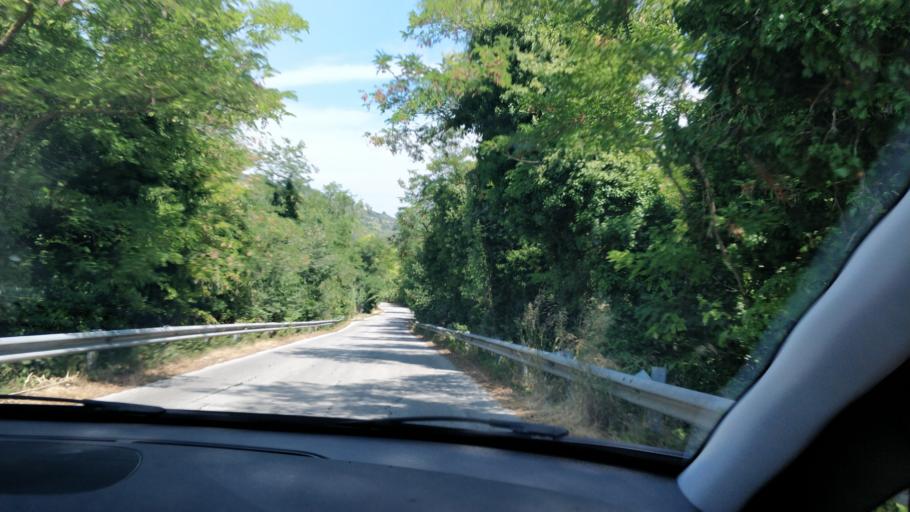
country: IT
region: Abruzzo
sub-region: Provincia di Chieti
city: Sambuceto
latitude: 42.4094
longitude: 14.2072
